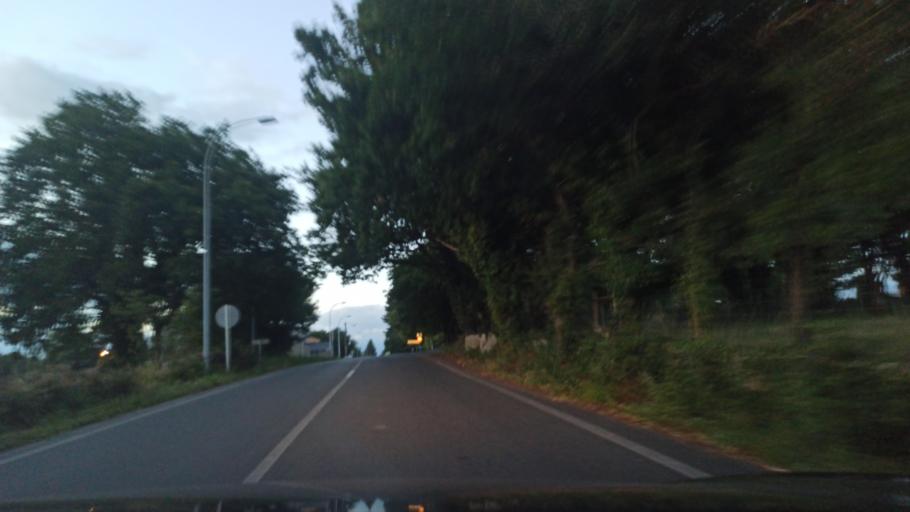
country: ES
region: Galicia
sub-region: Provincia de Lugo
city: Lugo
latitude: 42.9847
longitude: -7.5827
